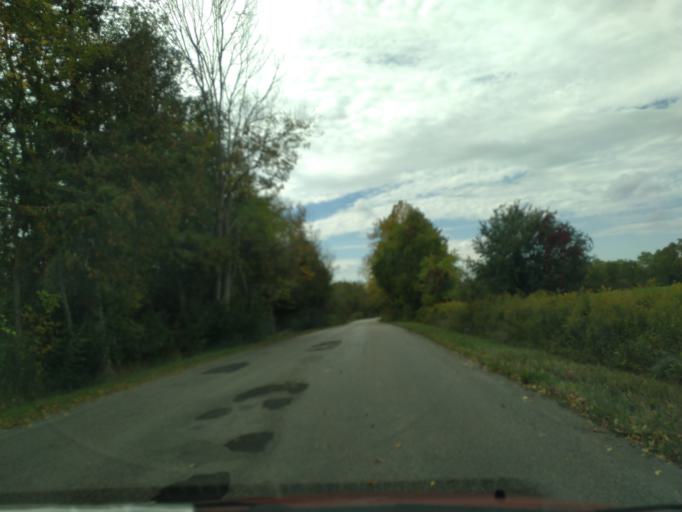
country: CA
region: Ontario
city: Keswick
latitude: 44.2609
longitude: -79.3482
